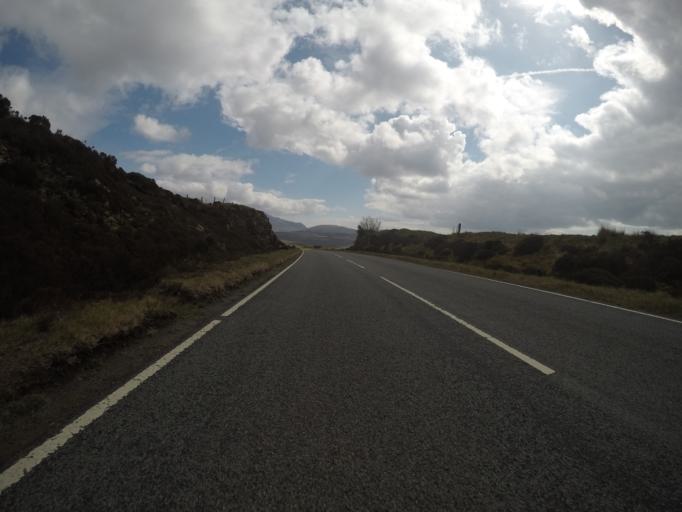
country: GB
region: Scotland
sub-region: Highland
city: Isle of Skye
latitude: 57.3118
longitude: -6.3191
